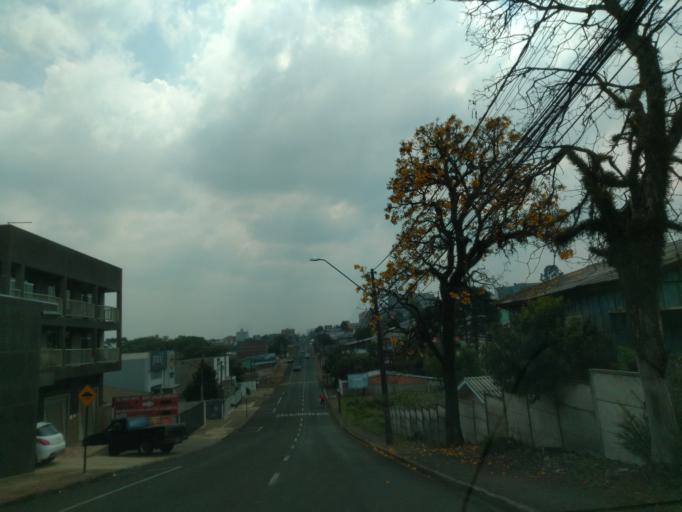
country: BR
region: Parana
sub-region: Guarapuava
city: Guarapuava
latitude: -25.3830
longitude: -51.4804
